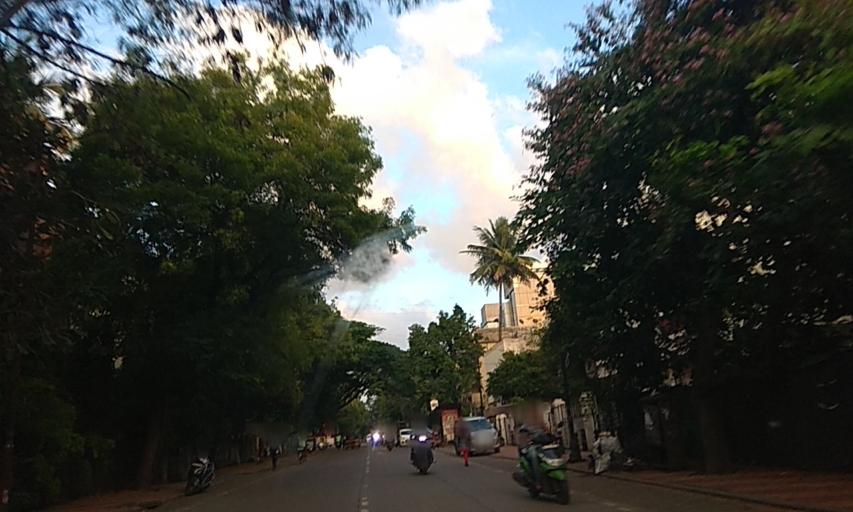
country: IN
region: Maharashtra
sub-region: Pune Division
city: Pune
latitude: 18.4925
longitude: 73.8527
